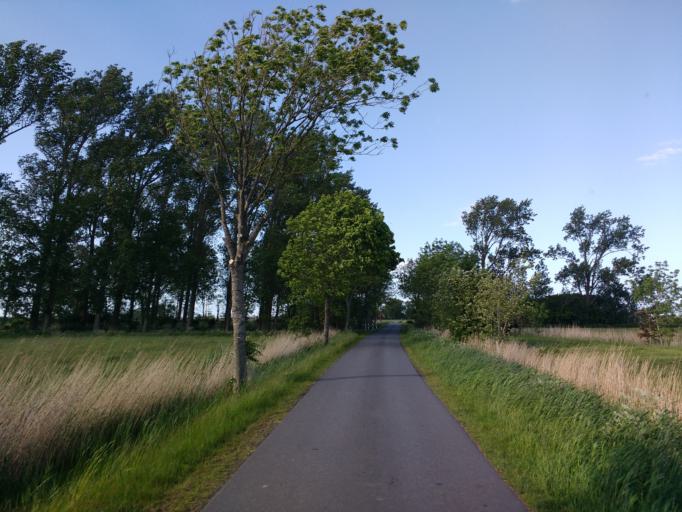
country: DE
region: Lower Saxony
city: Schillig
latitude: 53.6800
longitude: 7.9313
